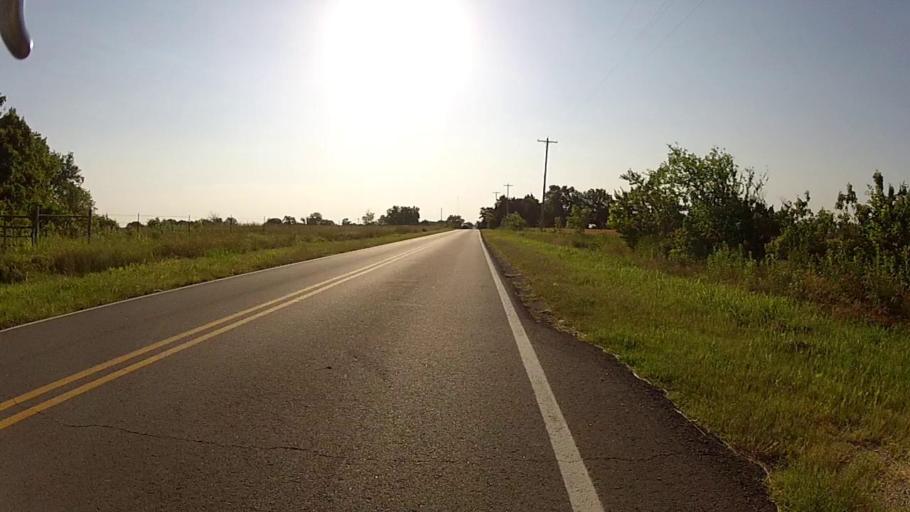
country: US
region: Kansas
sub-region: Montgomery County
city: Caney
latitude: 37.0963
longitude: -95.9333
